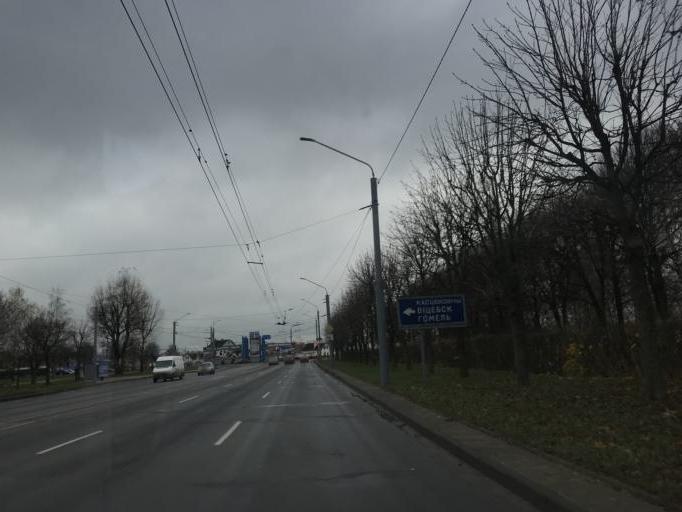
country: BY
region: Mogilev
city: Mahilyow
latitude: 53.8630
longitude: 30.3349
